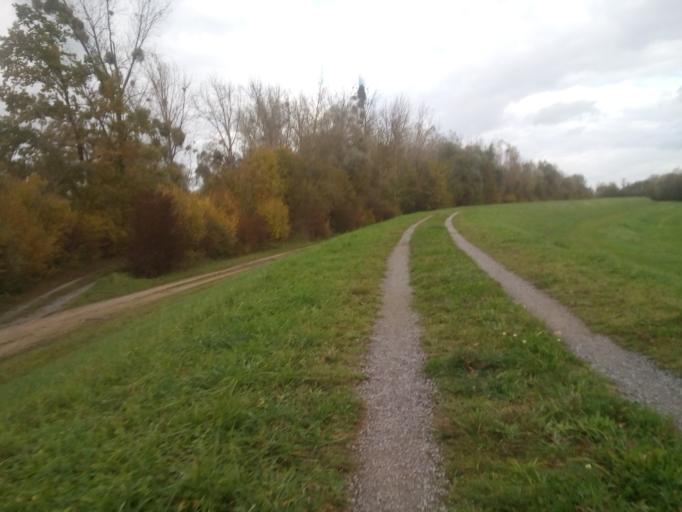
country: DE
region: Baden-Wuerttemberg
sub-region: Karlsruhe Region
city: Schwarzach
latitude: 48.7852
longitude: 8.0464
